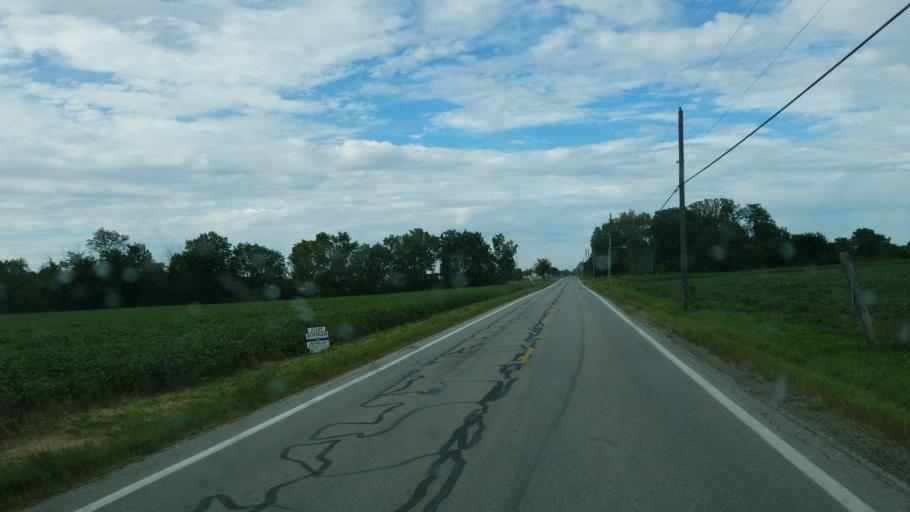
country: US
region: Ohio
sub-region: Delaware County
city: Sunbury
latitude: 40.1863
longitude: -82.8059
